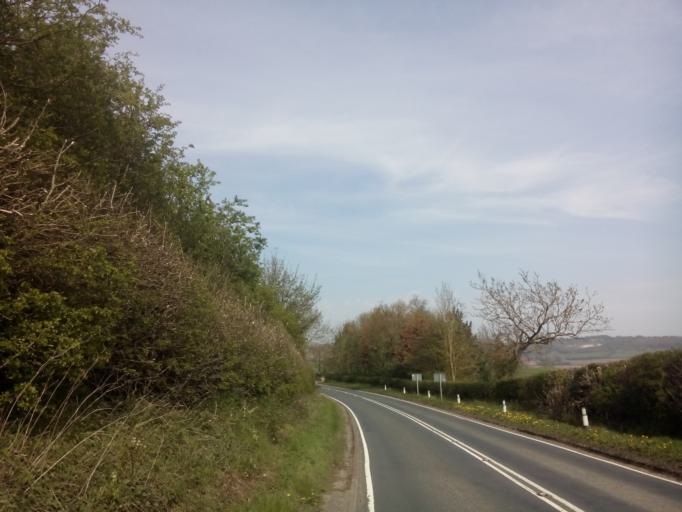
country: GB
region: England
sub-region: County Durham
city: West Rainton
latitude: 54.7945
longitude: -1.5082
